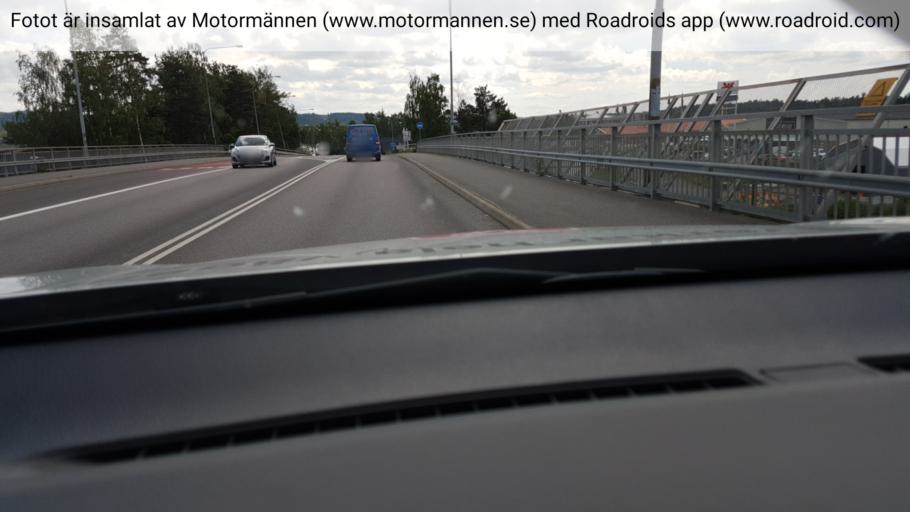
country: SE
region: Joenkoeping
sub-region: Jonkopings Kommun
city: Jonkoping
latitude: 57.7637
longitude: 14.1680
